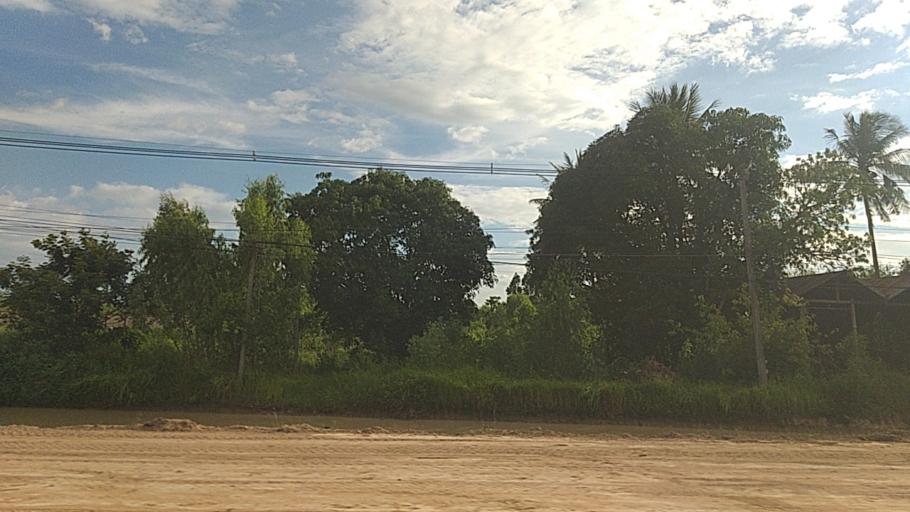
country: TH
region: Surin
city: Kap Choeng
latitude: 14.4882
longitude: 103.5766
